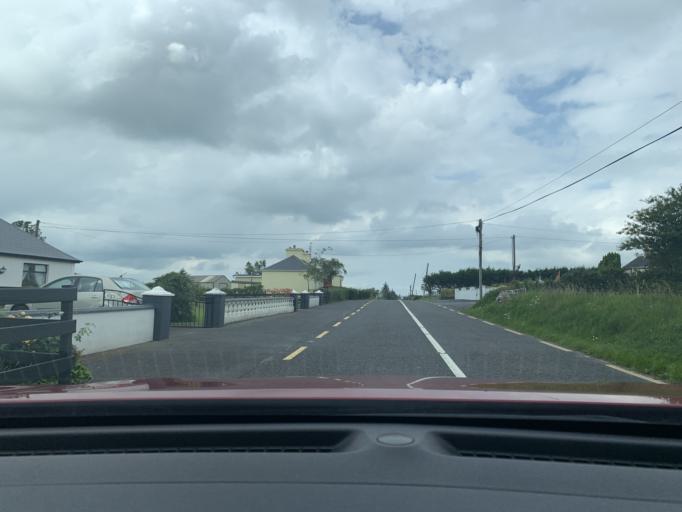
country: IE
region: Connaught
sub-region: Maigh Eo
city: Swinford
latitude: 53.8595
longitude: -8.8716
